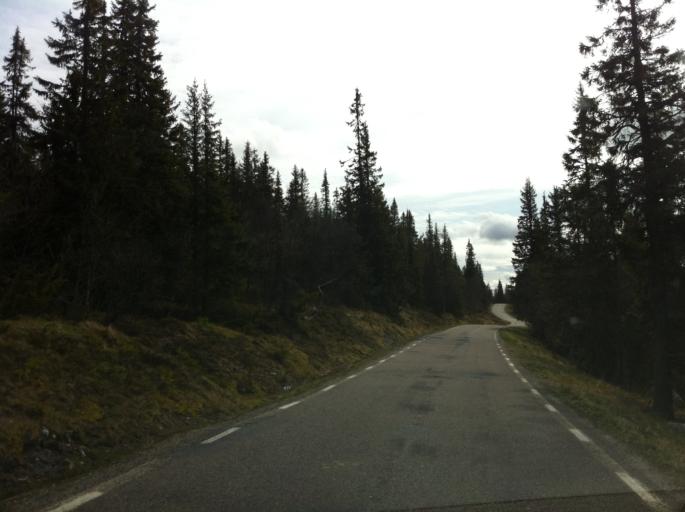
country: NO
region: Hedmark
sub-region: Engerdal
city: Engerdal
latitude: 62.3009
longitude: 12.8022
